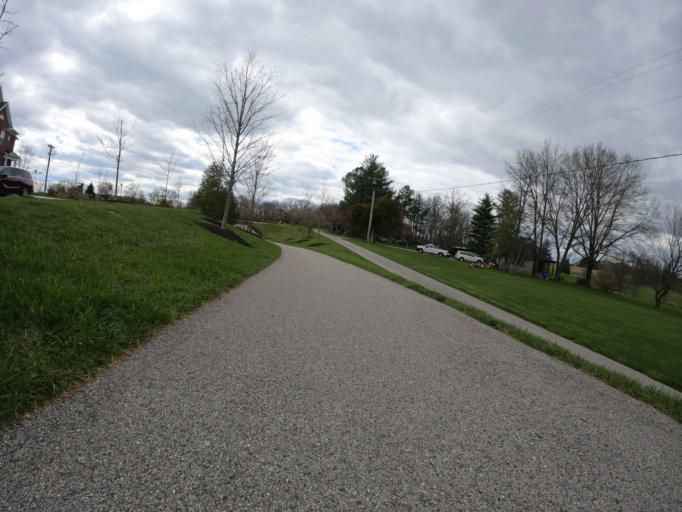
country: US
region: Maryland
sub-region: Howard County
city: North Laurel
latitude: 39.1478
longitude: -76.8542
